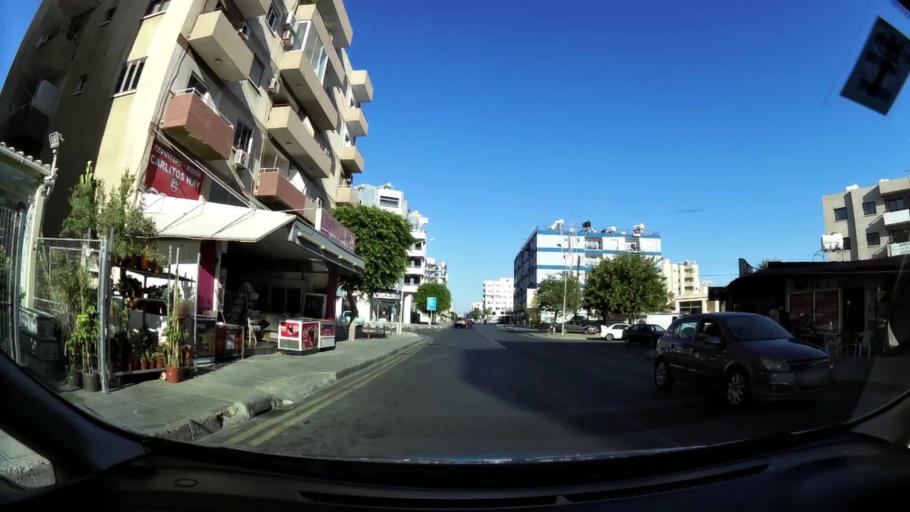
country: CY
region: Larnaka
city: Larnaca
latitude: 34.9194
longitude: 33.6178
